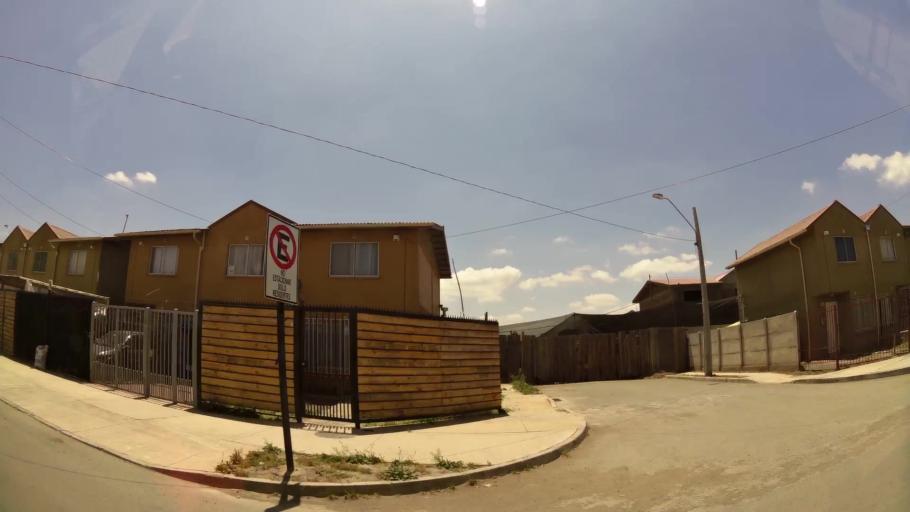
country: CL
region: Santiago Metropolitan
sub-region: Provincia de Talagante
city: Penaflor
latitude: -33.5742
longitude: -70.8009
